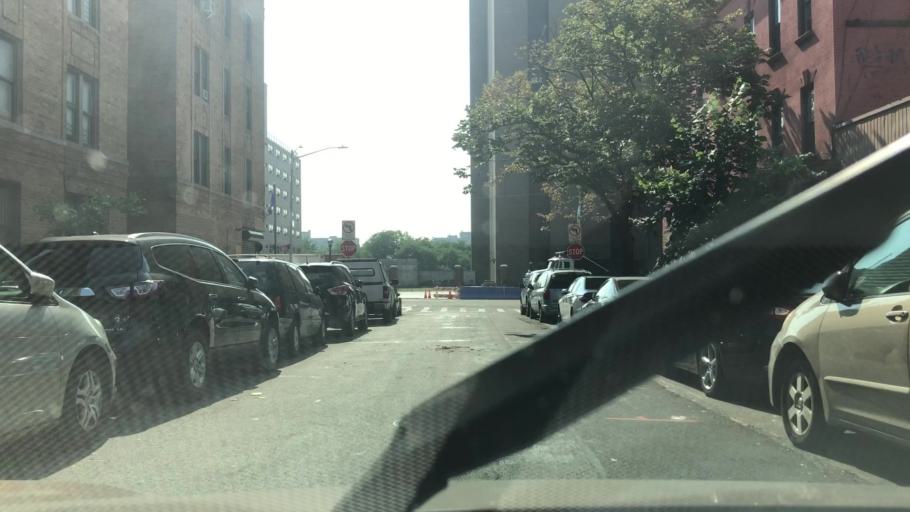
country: US
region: New York
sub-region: New York County
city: Inwood
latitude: 40.8501
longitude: -73.9301
